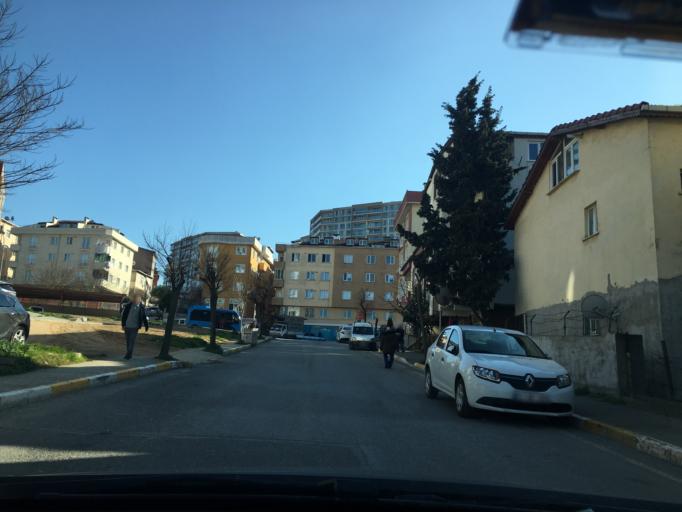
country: TR
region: Istanbul
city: Icmeler
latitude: 40.8658
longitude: 29.3033
